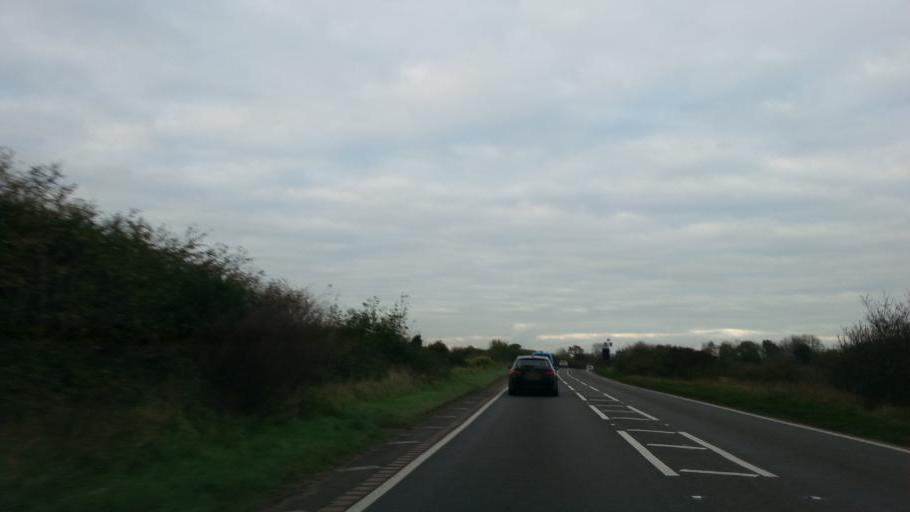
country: GB
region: England
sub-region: District of Rutland
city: Ketton
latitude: 52.5754
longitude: -0.5671
